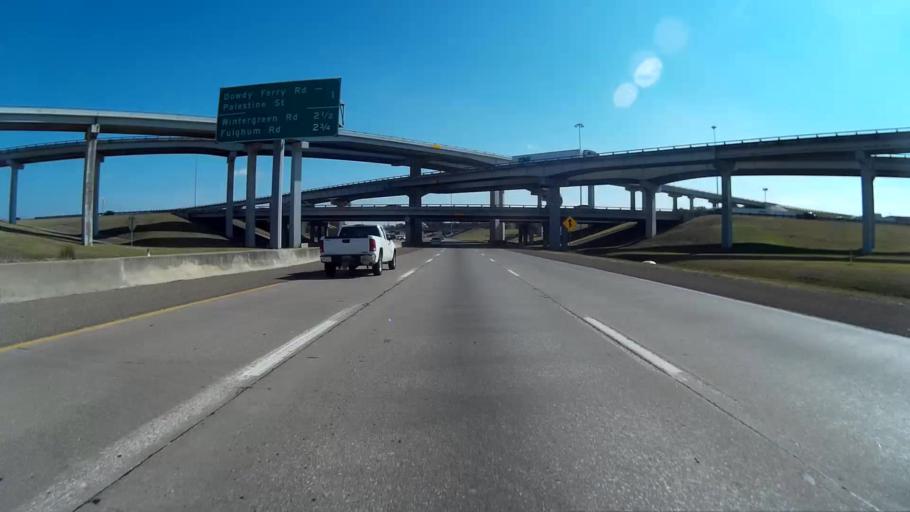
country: US
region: Texas
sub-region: Dallas County
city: Hutchins
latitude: 32.6625
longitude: -96.7274
